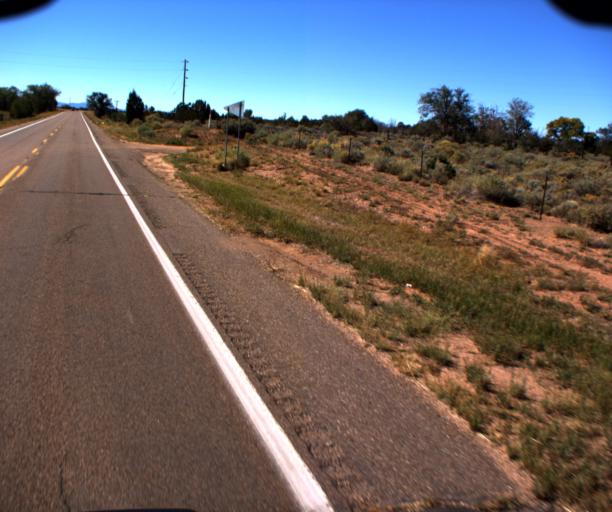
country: US
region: Arizona
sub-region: Apache County
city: Saint Johns
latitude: 34.4829
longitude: -109.3832
